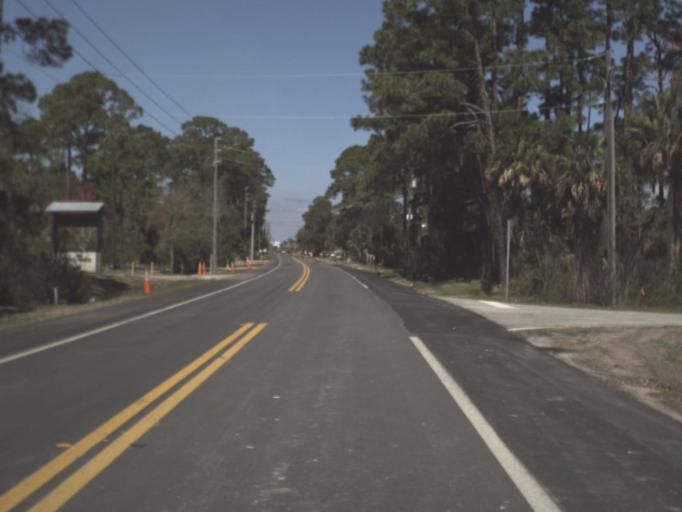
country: US
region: Florida
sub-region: Gulf County
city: Port Saint Joe
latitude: 29.7433
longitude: -85.3015
